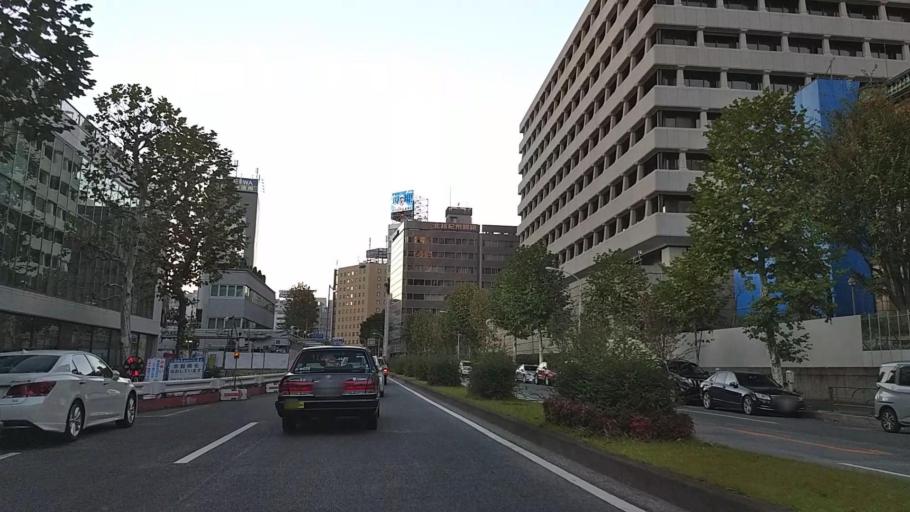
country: JP
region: Tokyo
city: Tokyo
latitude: 35.6857
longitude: 139.7710
